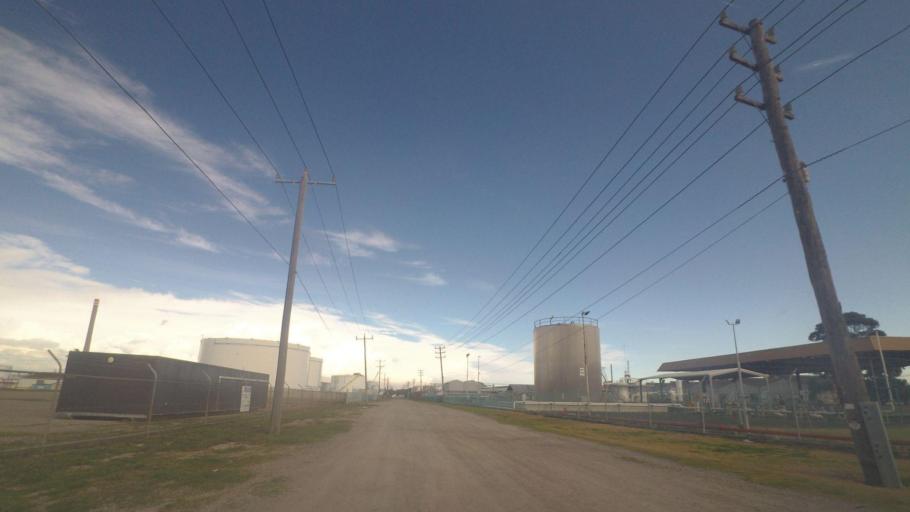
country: AU
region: Victoria
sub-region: Hobsons Bay
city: Spotswood
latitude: -37.8328
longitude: 144.8894
